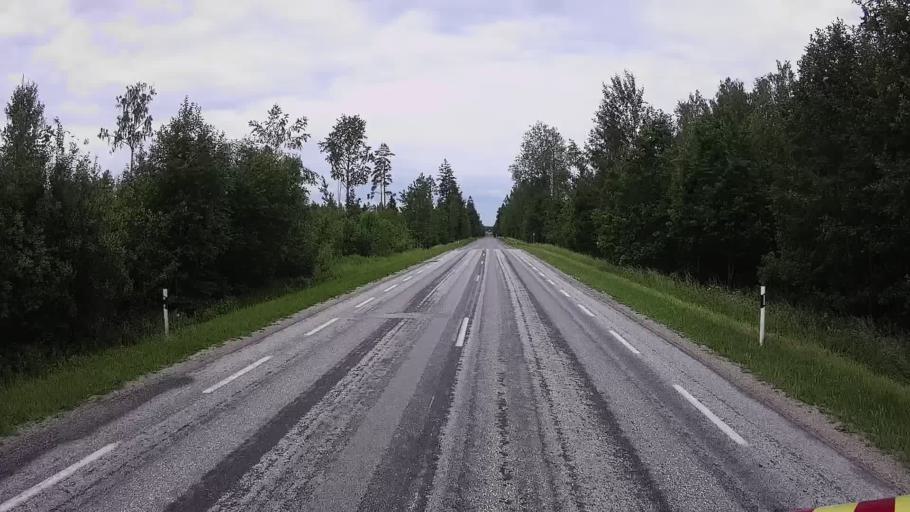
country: EE
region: Viljandimaa
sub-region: Karksi vald
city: Karksi-Nuia
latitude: 58.1915
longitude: 25.6065
